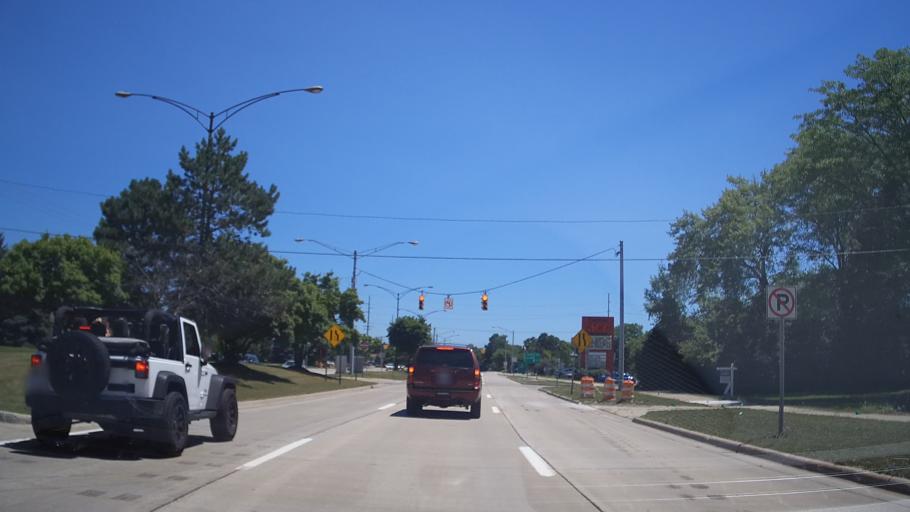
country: US
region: Michigan
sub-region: Oakland County
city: Troy
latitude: 42.5914
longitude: -83.1519
